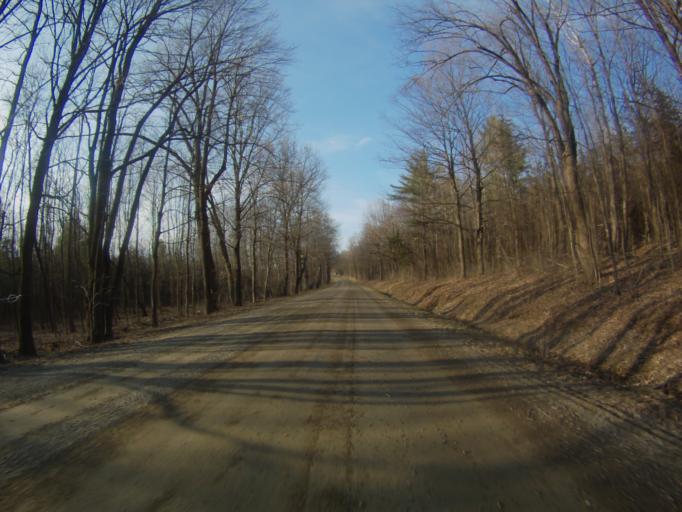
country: US
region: Vermont
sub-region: Addison County
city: Vergennes
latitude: 44.0503
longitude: -73.2919
